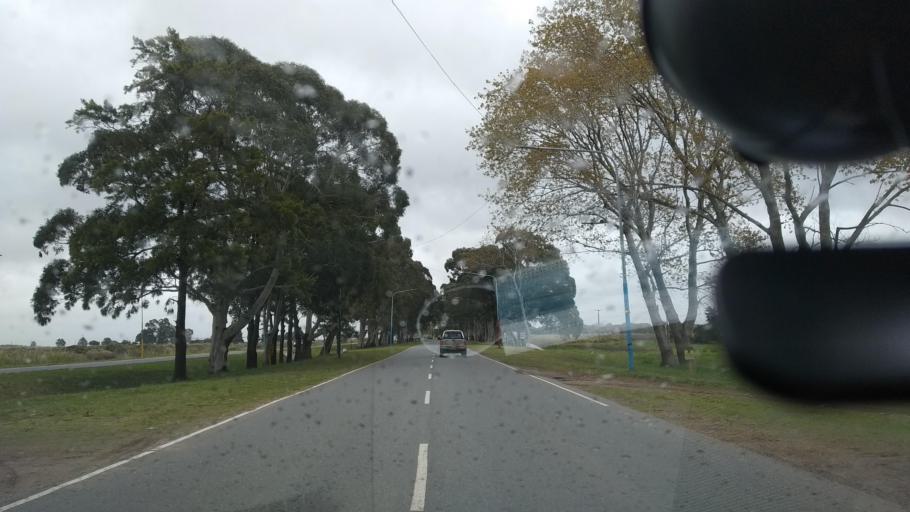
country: AR
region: Buenos Aires
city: San Clemente del Tuyu
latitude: -36.3867
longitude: -56.7302
